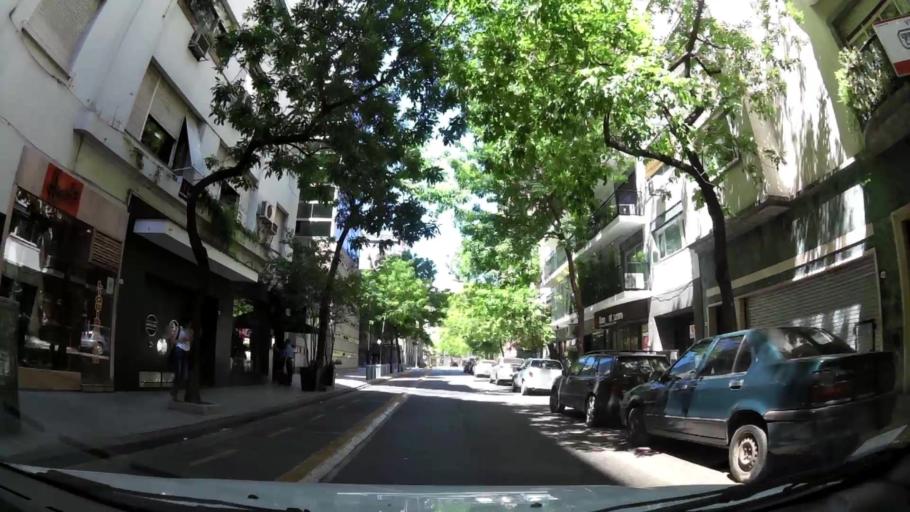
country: AR
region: Buenos Aires F.D.
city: Retiro
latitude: -34.5941
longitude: -58.3795
